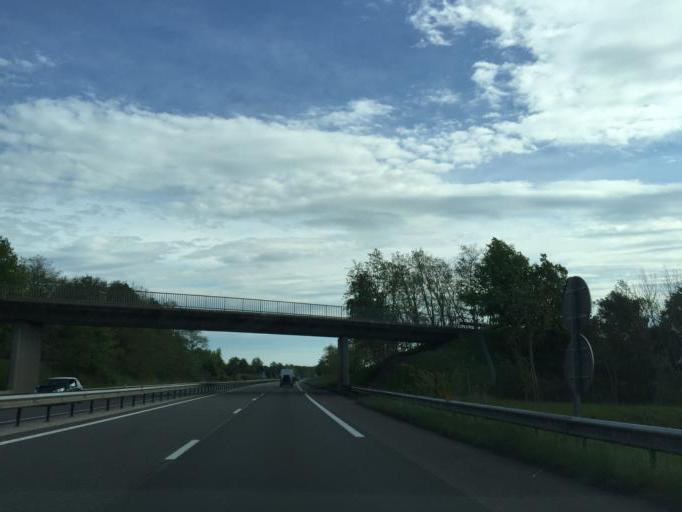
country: FR
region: Rhone-Alpes
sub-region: Departement de la Loire
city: Montrond-les-Bains
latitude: 45.6902
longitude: 4.1565
